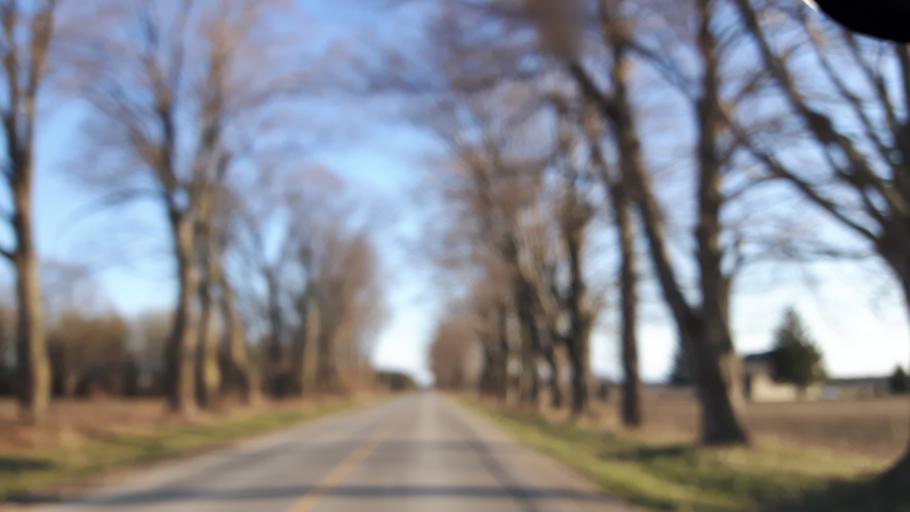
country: CA
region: Ontario
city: Goderich
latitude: 43.6949
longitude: -81.6849
